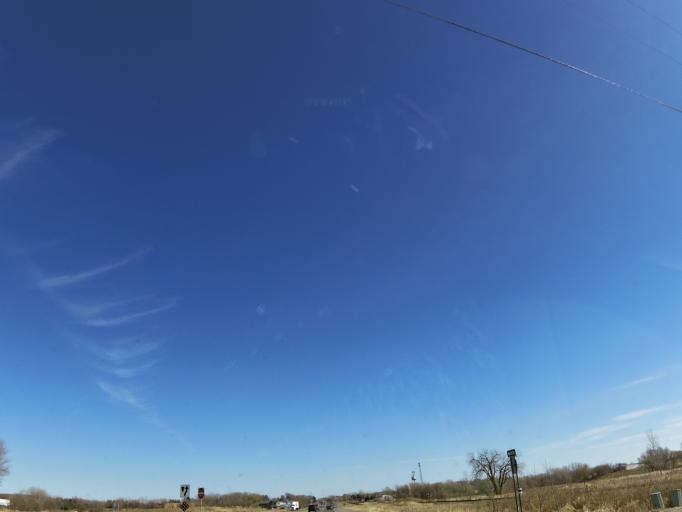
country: US
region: Minnesota
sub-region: Hennepin County
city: Medina
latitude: 45.0488
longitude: -93.5534
